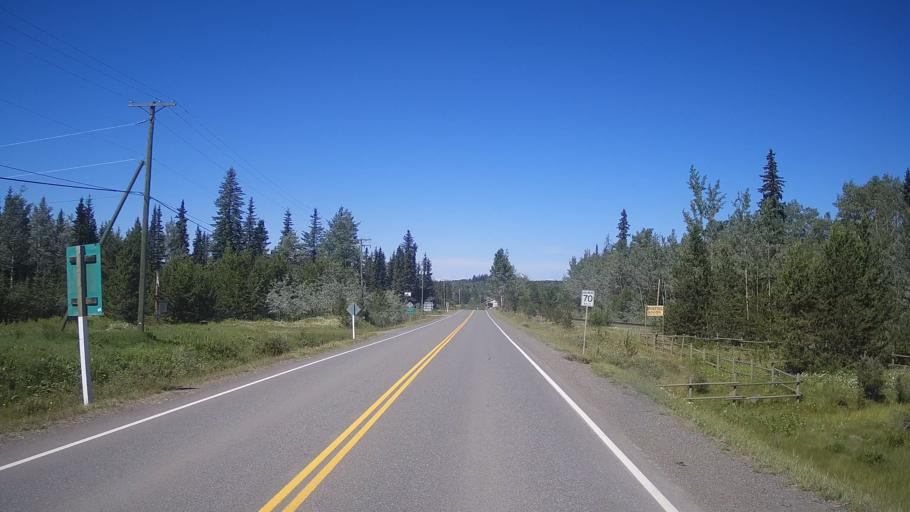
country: CA
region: British Columbia
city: Cache Creek
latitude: 51.5544
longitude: -121.1959
